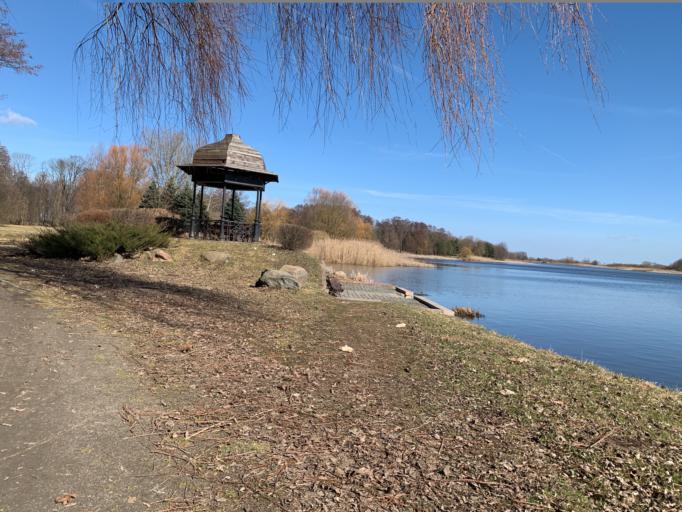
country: BY
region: Minsk
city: Nyasvizh
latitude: 53.2278
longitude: 26.6977
